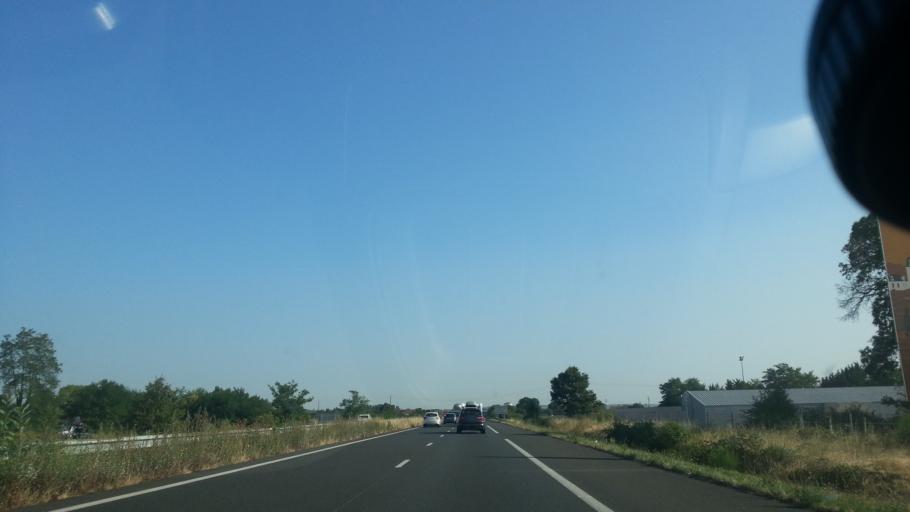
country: FR
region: Poitou-Charentes
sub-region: Departement de la Vienne
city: Chatellerault
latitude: 46.8071
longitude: 0.5136
